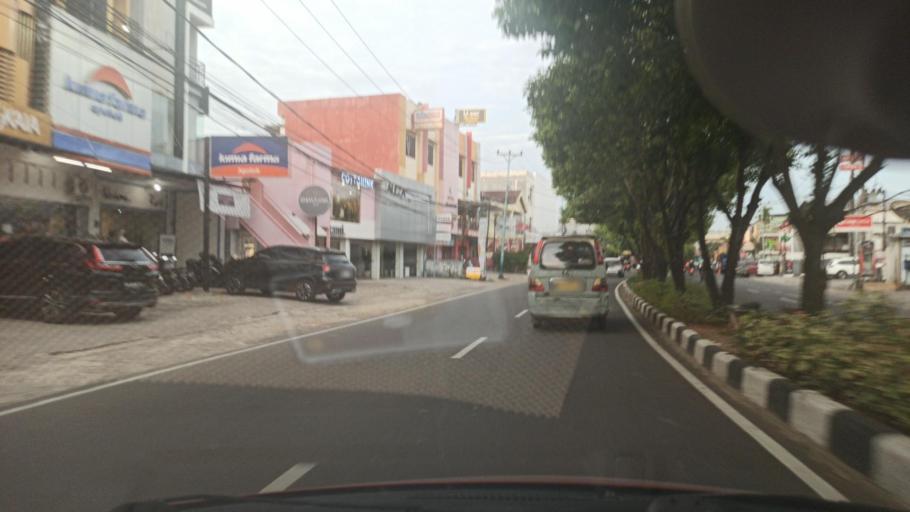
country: ID
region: South Sumatra
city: Palembang
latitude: -2.9742
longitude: 104.7380
